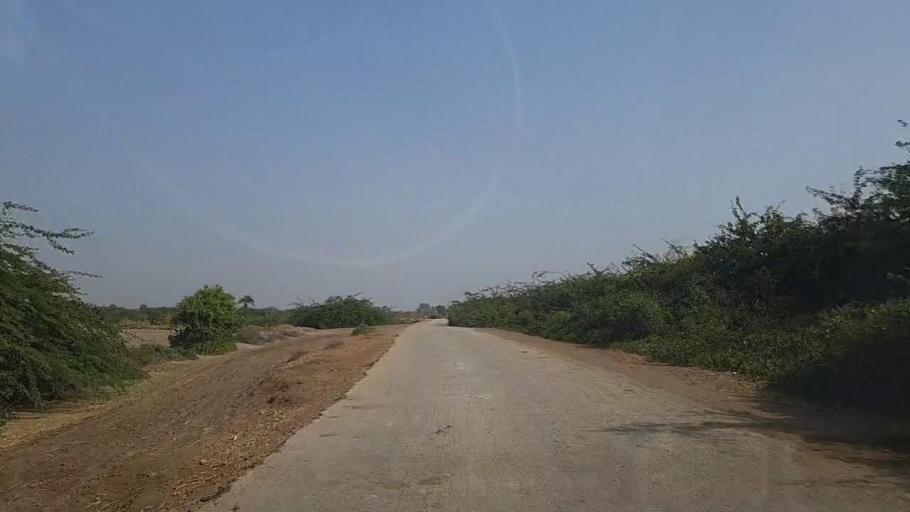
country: PK
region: Sindh
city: Keti Bandar
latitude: 24.2433
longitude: 67.7025
